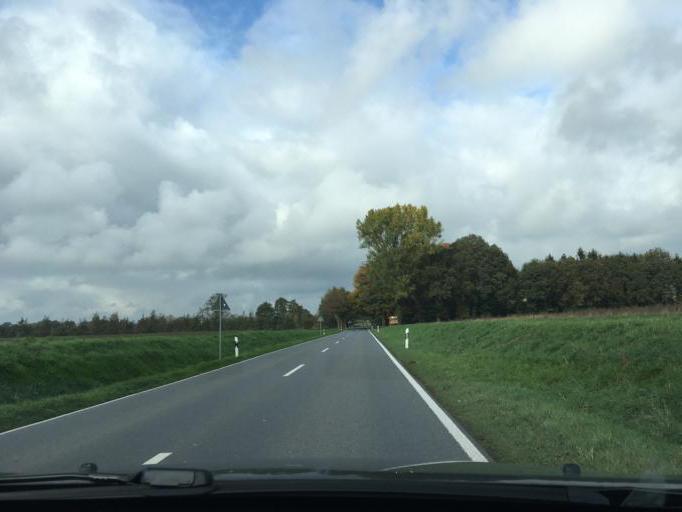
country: DE
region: North Rhine-Westphalia
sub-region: Regierungsbezirk Munster
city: Vreden
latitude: 52.0571
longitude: 6.7661
